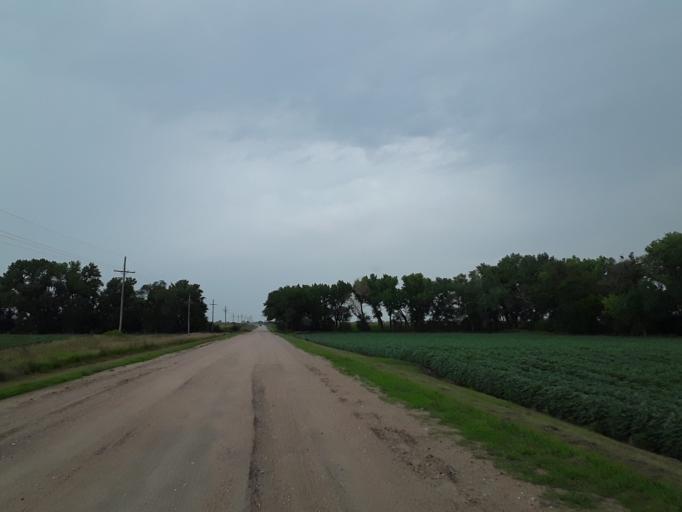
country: US
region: Nebraska
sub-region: Saunders County
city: Yutan
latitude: 41.1652
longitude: -96.4449
